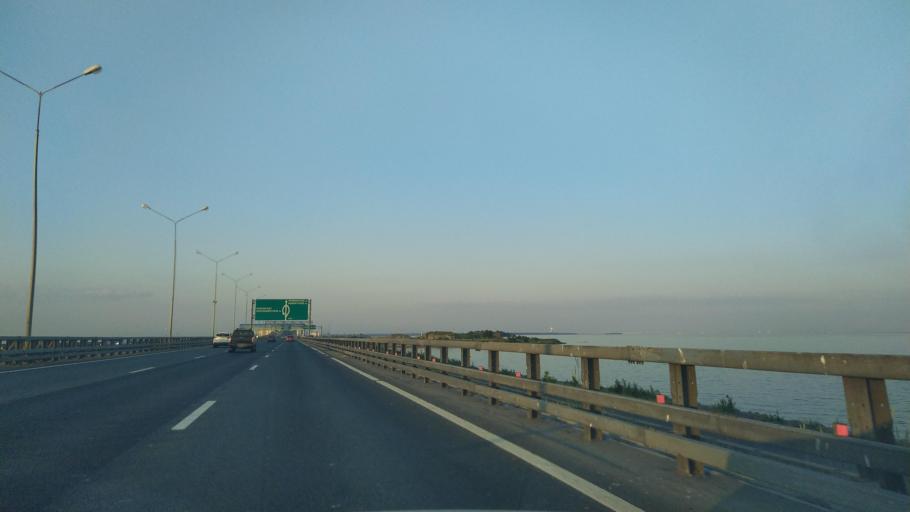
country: RU
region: St.-Petersburg
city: Kronshtadt
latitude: 60.0241
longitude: 29.8089
